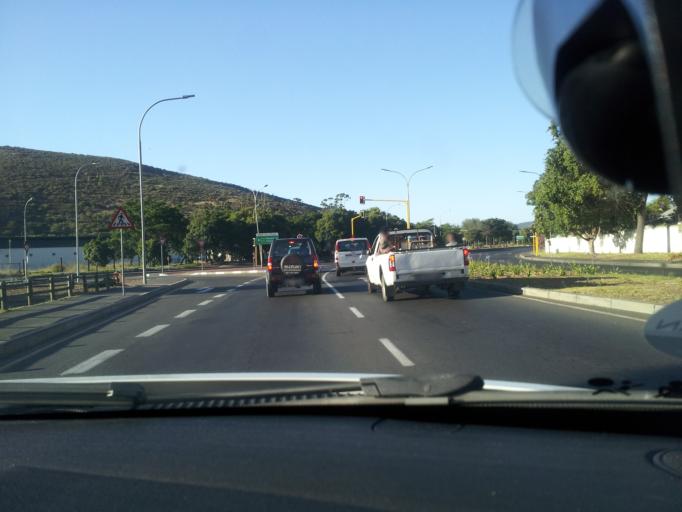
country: ZA
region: Western Cape
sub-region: Cape Winelands District Municipality
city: Stellenbosch
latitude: -33.9379
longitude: 18.8515
